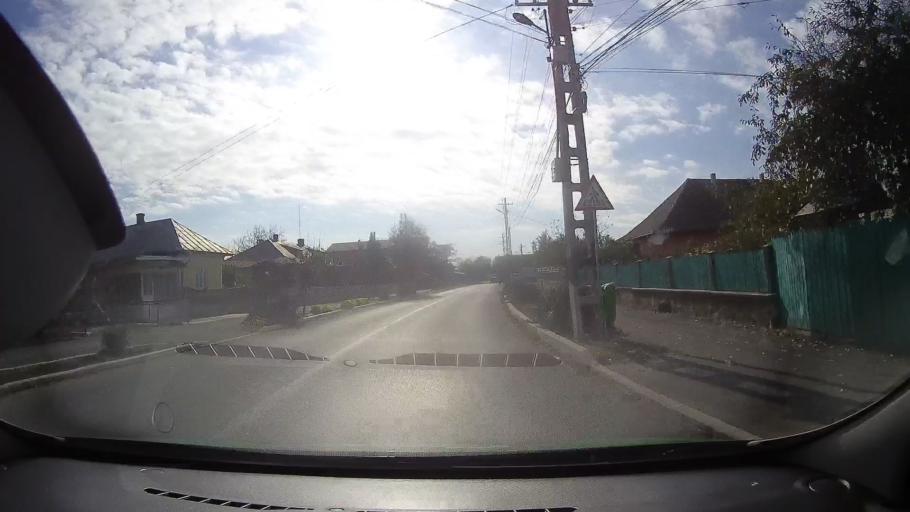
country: RO
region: Tulcea
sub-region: Comuna Sarichioi
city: Sarichioi
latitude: 44.9443
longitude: 28.8537
